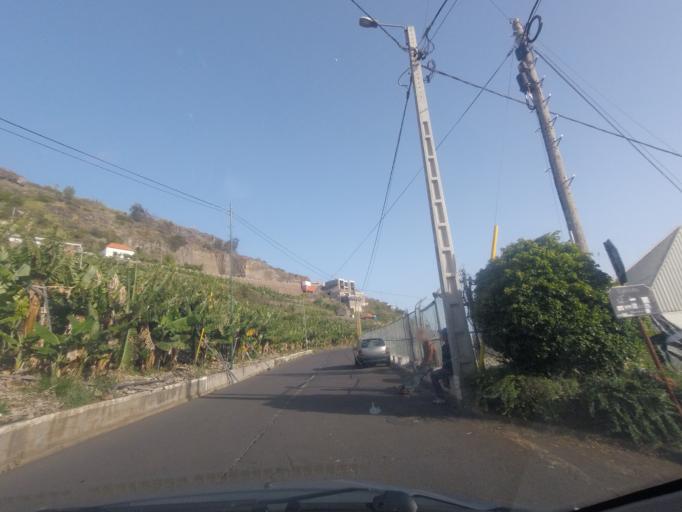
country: PT
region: Madeira
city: Ponta do Sol
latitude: 32.6816
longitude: -17.0731
